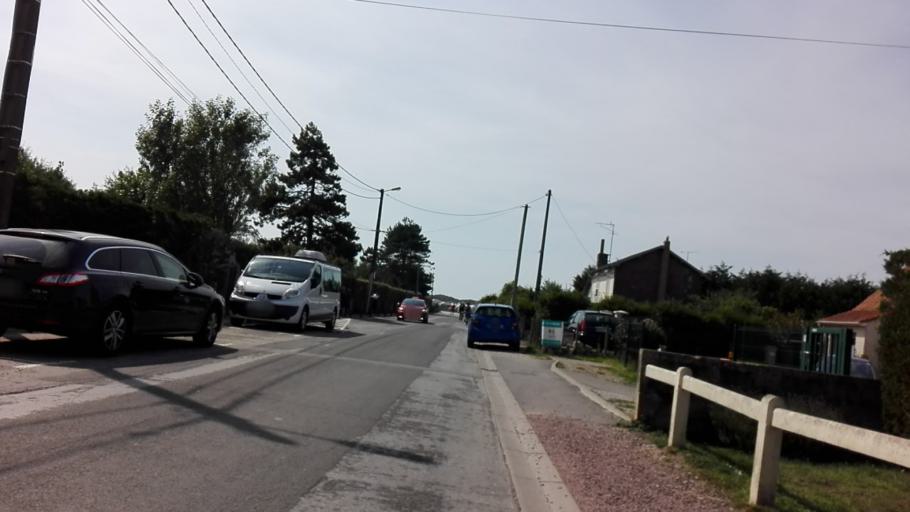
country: FR
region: Nord-Pas-de-Calais
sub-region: Departement du Pas-de-Calais
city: Berck-Plage
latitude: 50.3981
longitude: 1.5665
